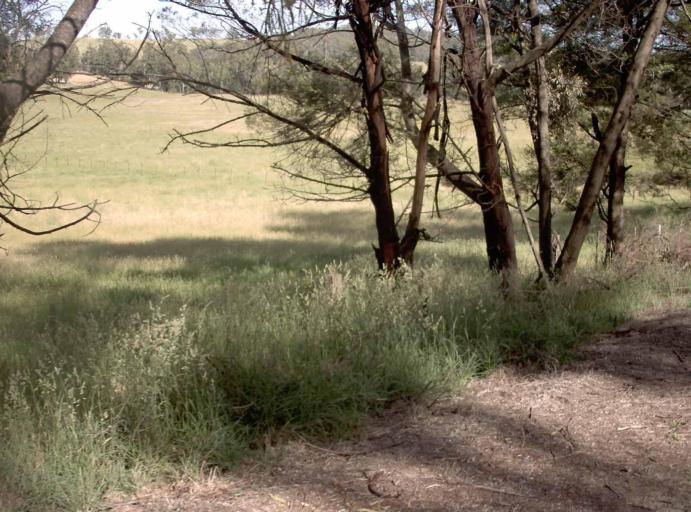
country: AU
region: Victoria
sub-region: East Gippsland
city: Lakes Entrance
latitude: -37.5422
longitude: 148.1485
